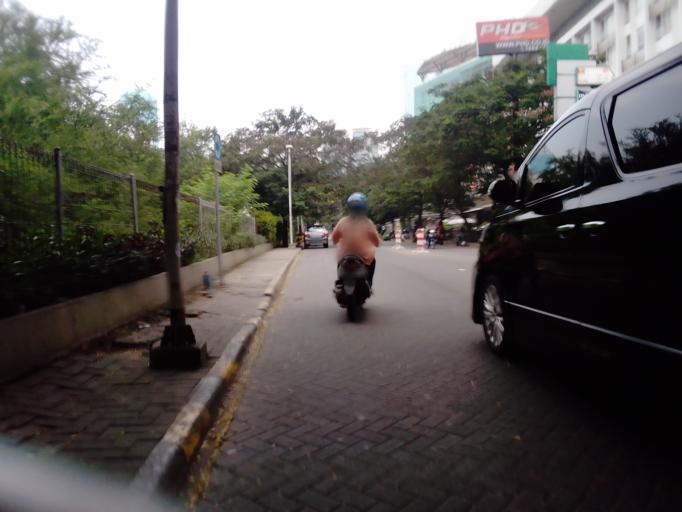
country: ID
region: Jakarta Raya
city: Jakarta
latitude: -6.1967
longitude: 106.8176
